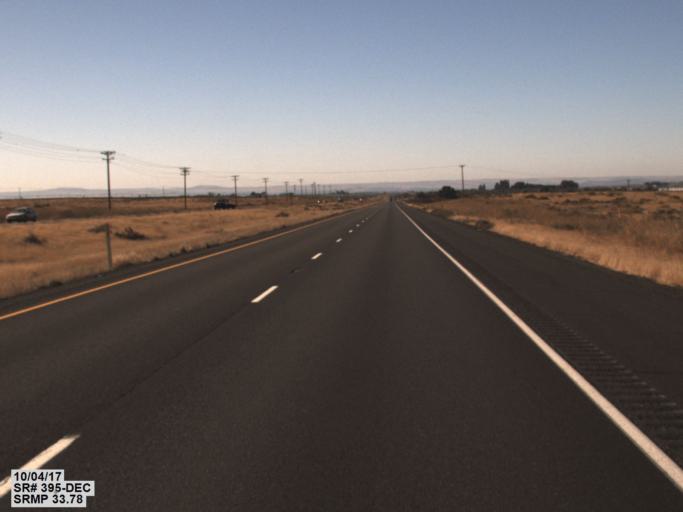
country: US
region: Washington
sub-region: Franklin County
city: Pasco
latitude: 46.4046
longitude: -119.0538
